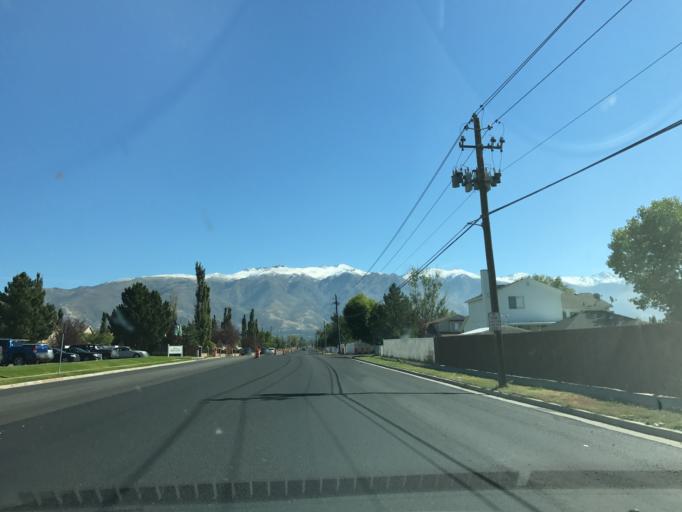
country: US
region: Utah
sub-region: Davis County
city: Hill Air Force Bace
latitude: 41.0892
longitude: -111.9701
